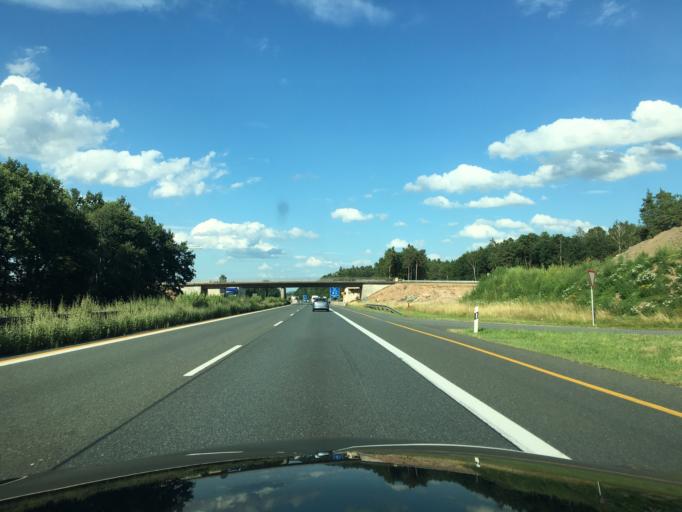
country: DE
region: Bavaria
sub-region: Regierungsbezirk Mittelfranken
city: Schwabach
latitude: 49.3138
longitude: 11.0305
